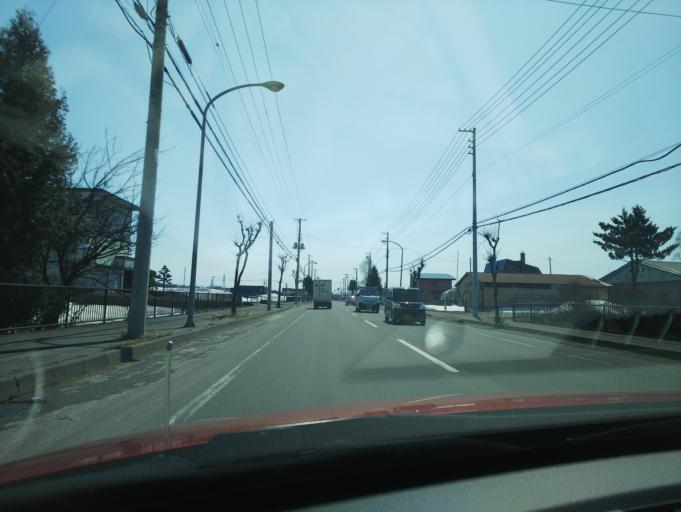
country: JP
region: Hokkaido
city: Nayoro
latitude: 44.3388
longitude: 142.4643
